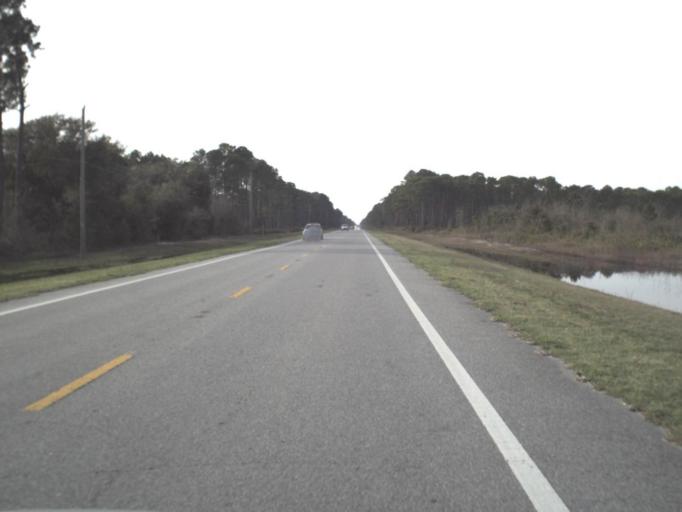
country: US
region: Florida
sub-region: Bay County
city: Tyndall Air Force Base
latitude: 30.0229
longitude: -85.5291
